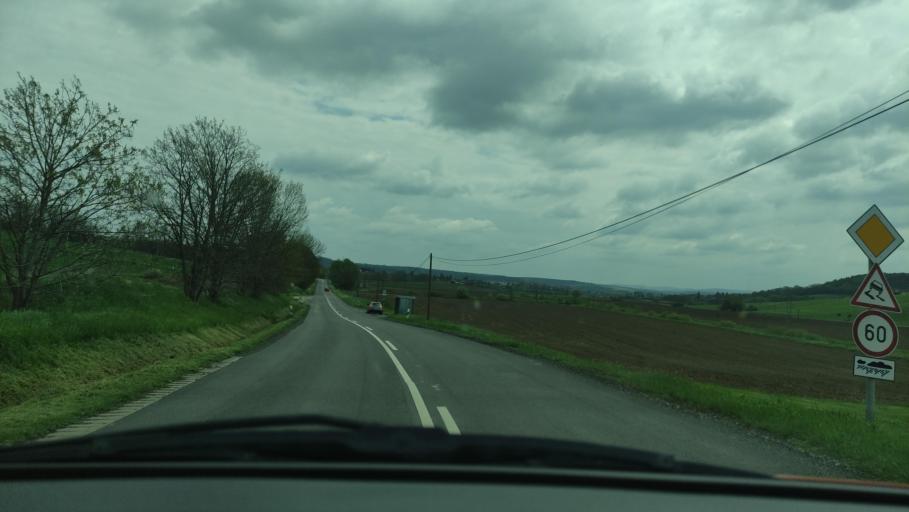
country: HU
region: Baranya
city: Sasd
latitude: 46.2662
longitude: 18.0788
